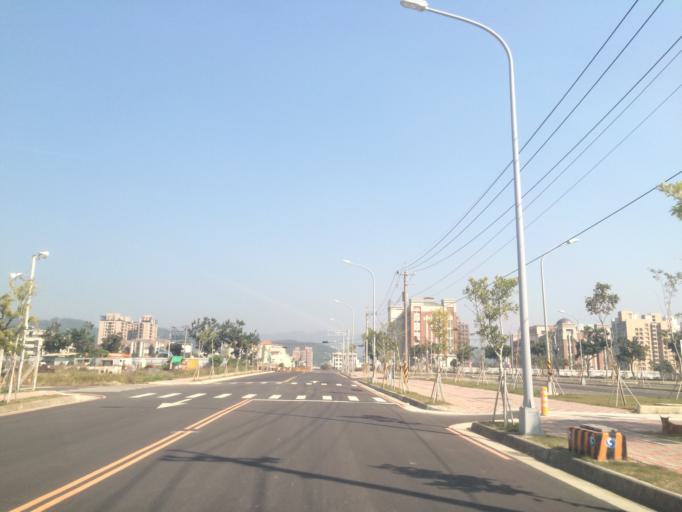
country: TW
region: Taiwan
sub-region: Taichung City
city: Taichung
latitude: 24.1801
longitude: 120.7086
